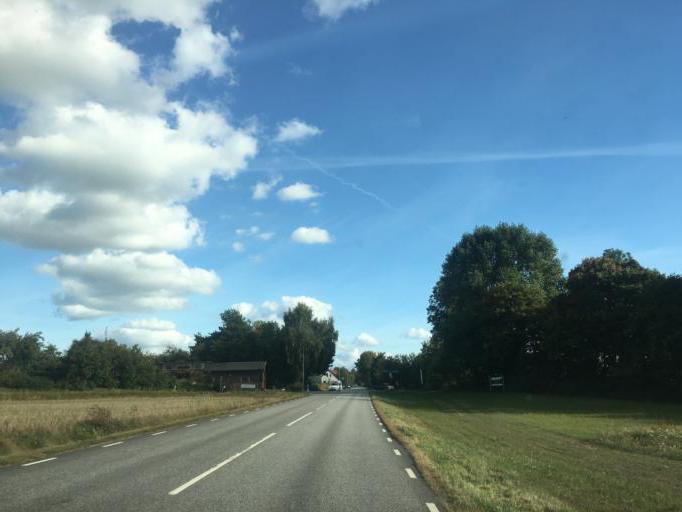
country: SE
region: Skane
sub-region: Hoors Kommun
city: Loberod
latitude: 55.7401
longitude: 13.4330
